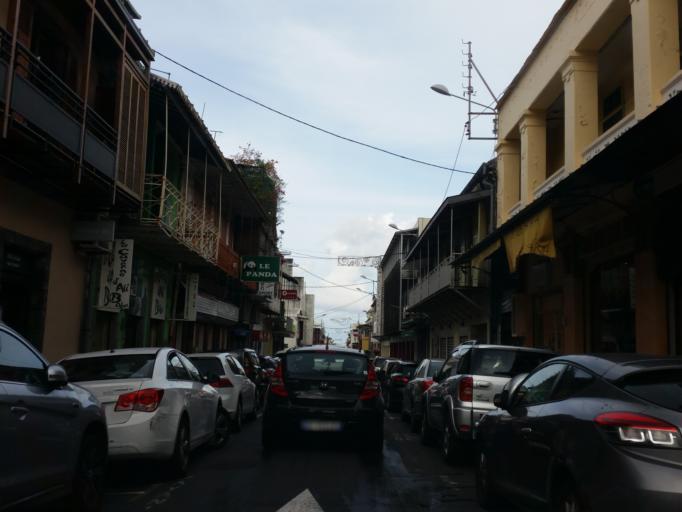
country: RE
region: Reunion
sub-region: Reunion
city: Saint-Denis
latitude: -20.8770
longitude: 55.4495
